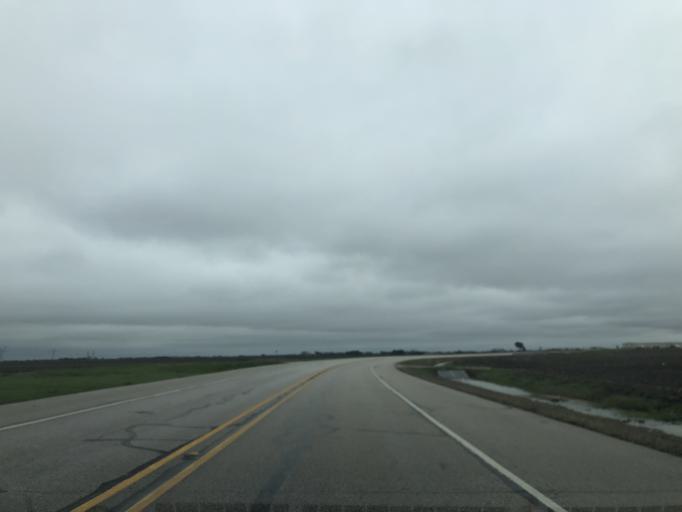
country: US
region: Texas
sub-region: Williamson County
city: Hutto
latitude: 30.6013
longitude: -97.5240
